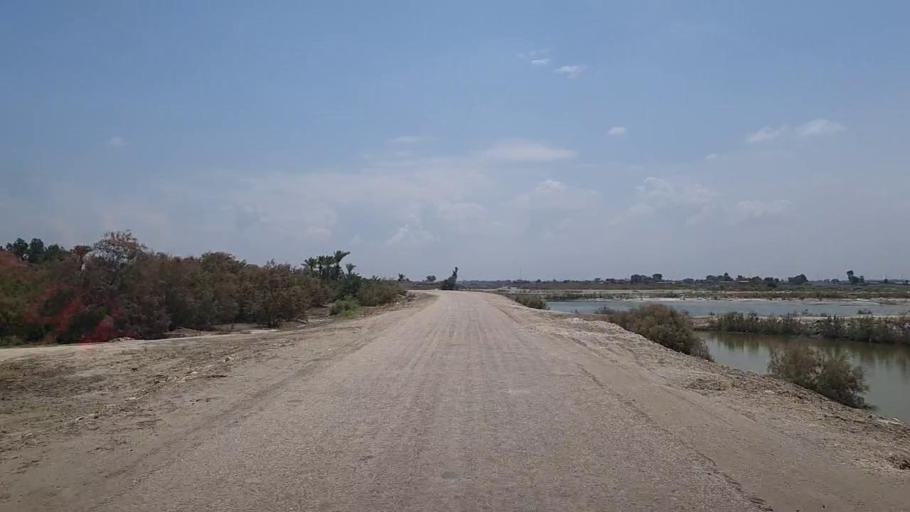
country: PK
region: Sindh
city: Kandhkot
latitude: 28.2815
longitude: 69.1703
